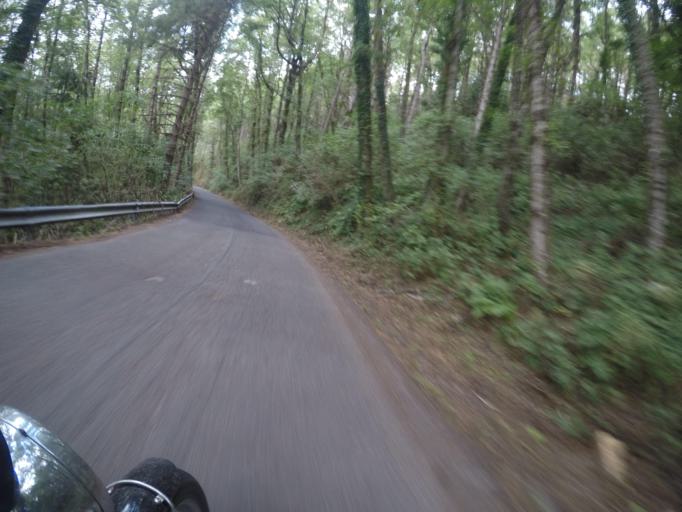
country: IT
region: Tuscany
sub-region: Provincia di Massa-Carrara
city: Carrara
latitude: 44.1179
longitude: 10.1027
